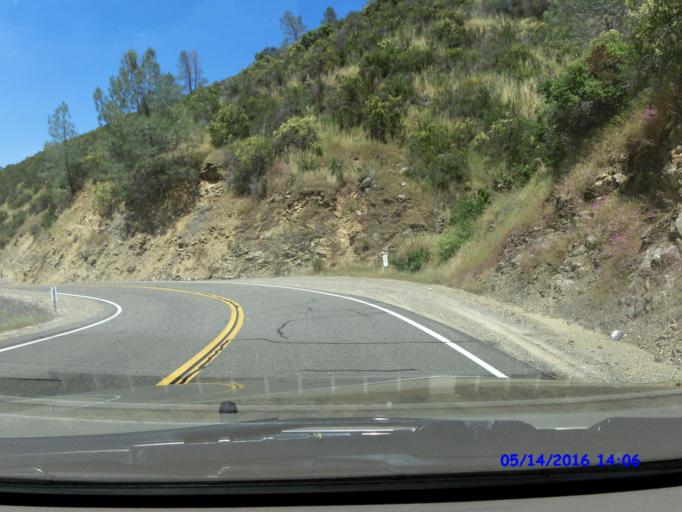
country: US
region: California
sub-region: Mariposa County
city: Mariposa
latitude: 37.6019
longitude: -120.1323
